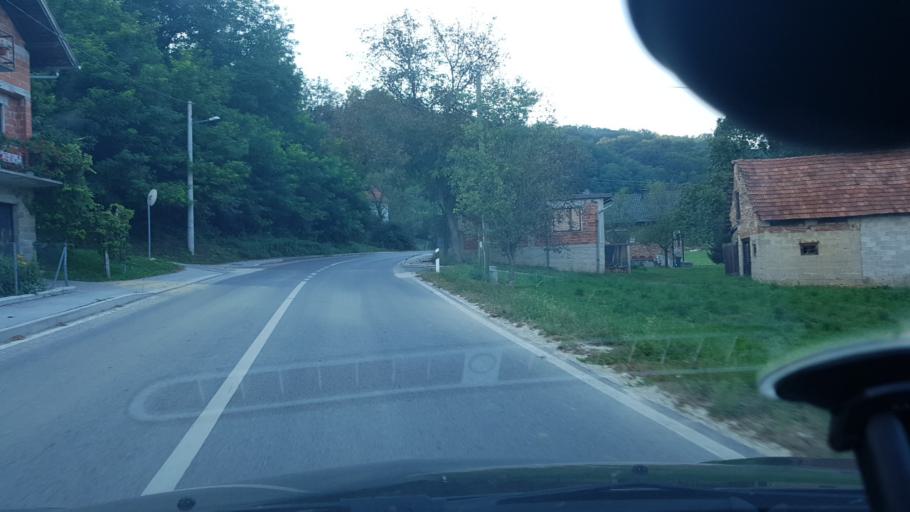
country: HR
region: Krapinsko-Zagorska
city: Pregrada
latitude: 46.1507
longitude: 15.7930
